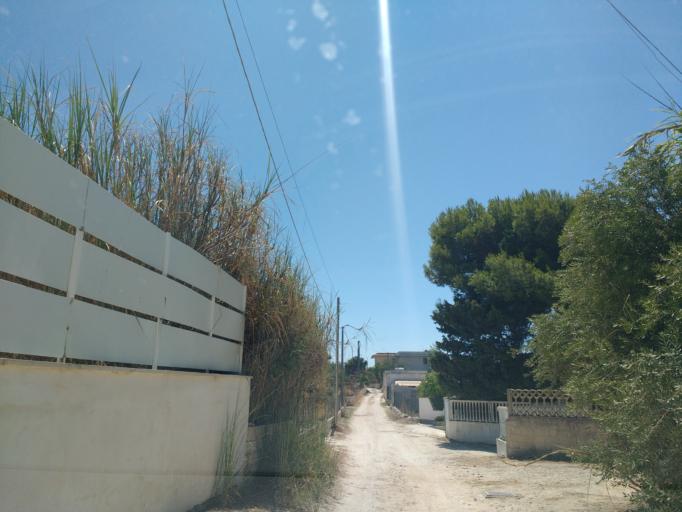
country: IT
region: Sicily
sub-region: Ragusa
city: Cava d'Aliga
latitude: 36.7269
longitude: 14.6915
